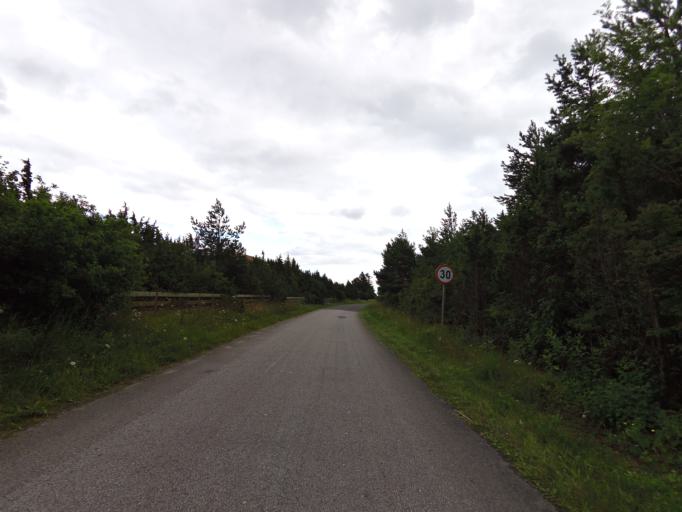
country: EE
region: Laeaene
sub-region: Vormsi vald
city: Hullo
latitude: 58.9744
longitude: 23.2610
